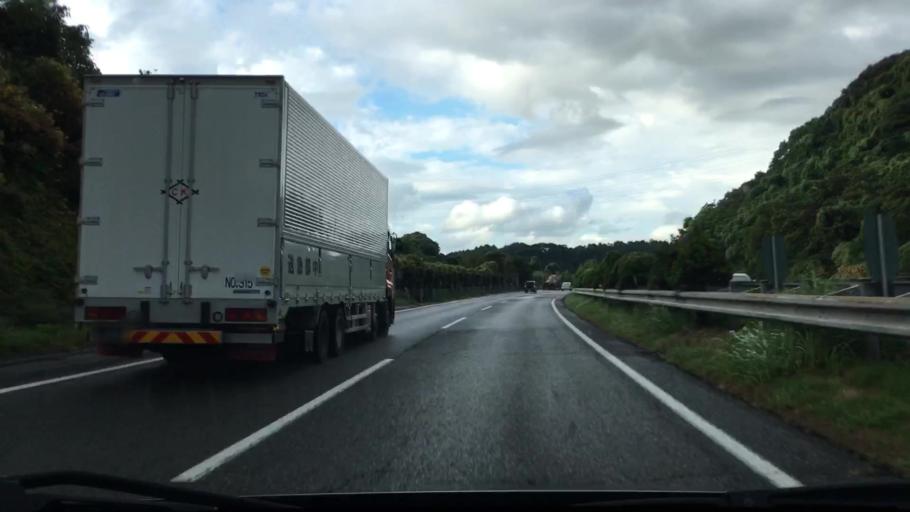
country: JP
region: Fukuoka
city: Koga
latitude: 33.7046
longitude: 130.4853
